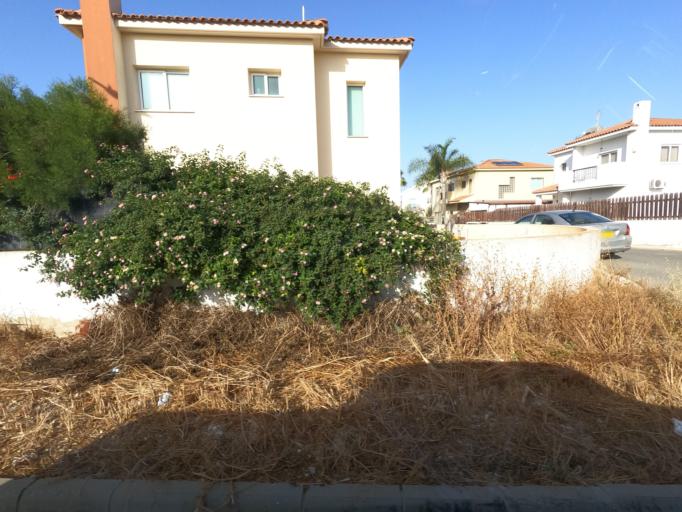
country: CY
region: Ammochostos
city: Liopetri
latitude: 34.9809
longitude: 33.9232
